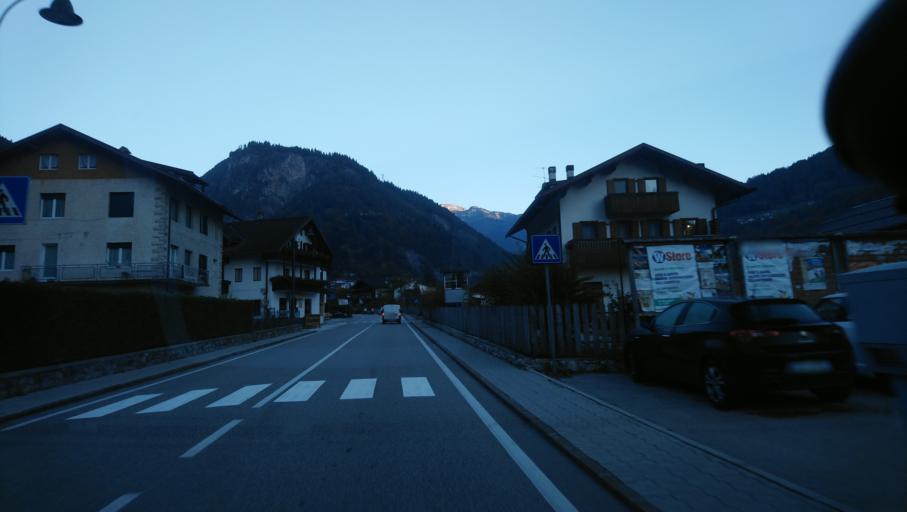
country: IT
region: Veneto
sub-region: Provincia di Belluno
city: Cencenighe Agordino
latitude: 46.3478
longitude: 11.9693
